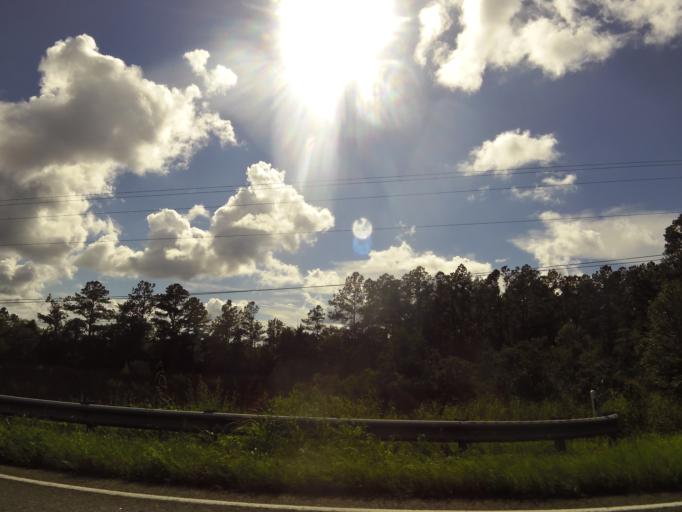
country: US
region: Georgia
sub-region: Camden County
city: Kingsland
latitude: 30.8332
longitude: -81.6969
